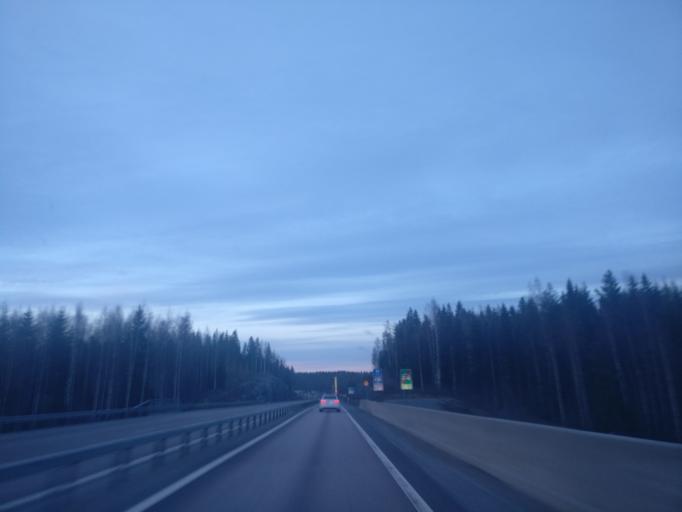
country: FI
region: Central Finland
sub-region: Jyvaeskylae
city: Saeynaetsalo
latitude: 62.2214
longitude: 25.8962
